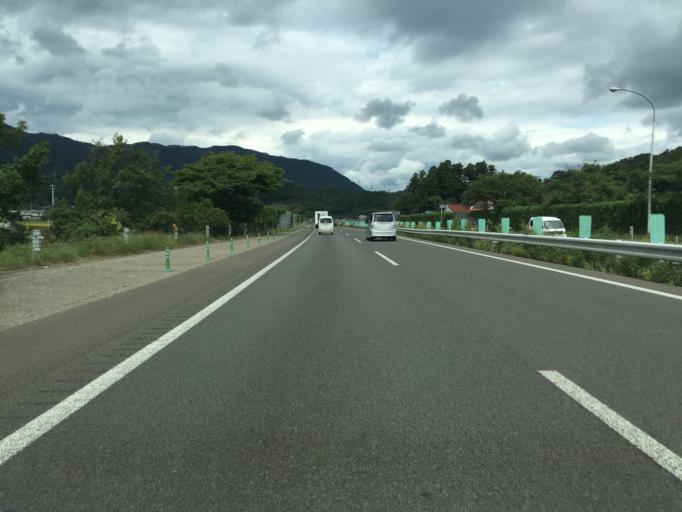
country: JP
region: Miyagi
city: Shiroishi
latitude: 37.9296
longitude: 140.6101
